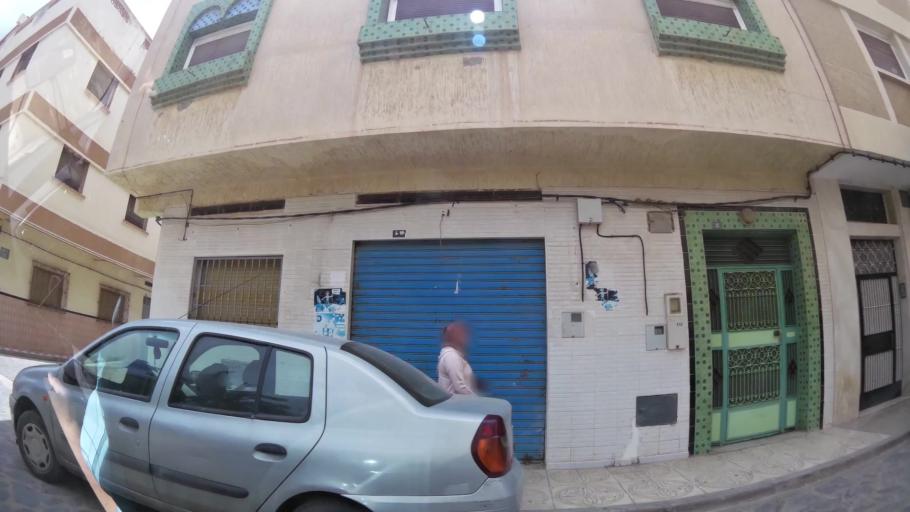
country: MA
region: Oriental
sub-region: Nador
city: Nador
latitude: 35.1644
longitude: -2.9253
